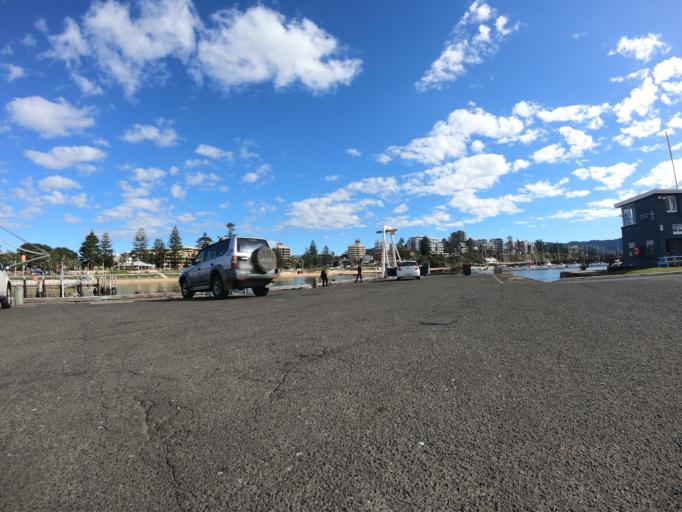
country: AU
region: New South Wales
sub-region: Wollongong
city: Wollongong
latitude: -34.4208
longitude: 150.9066
